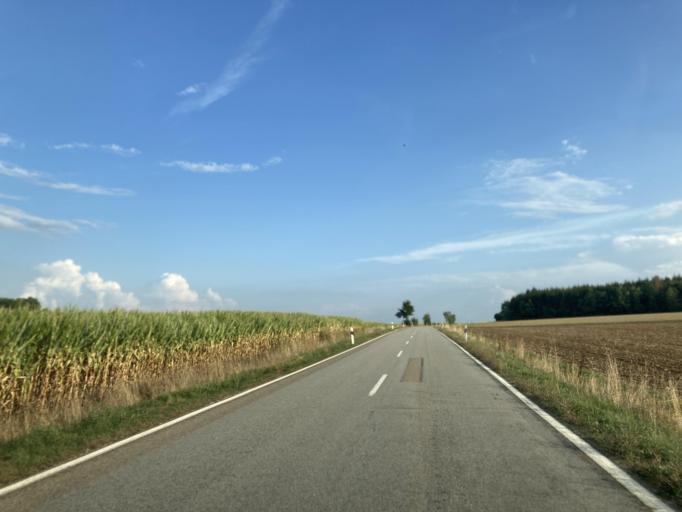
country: DE
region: Bavaria
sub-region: Swabia
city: Forheim
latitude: 48.7457
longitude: 10.4033
